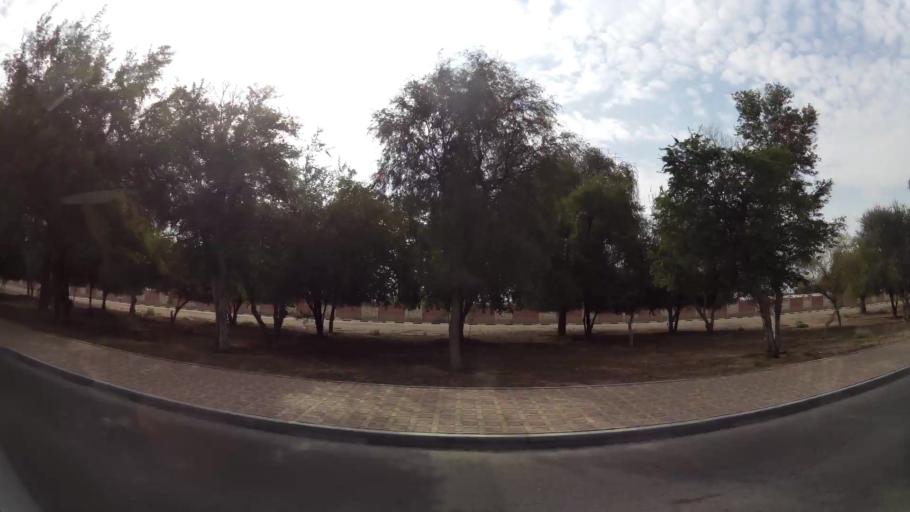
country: AE
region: Abu Dhabi
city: Al Ain
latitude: 24.2152
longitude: 55.7037
